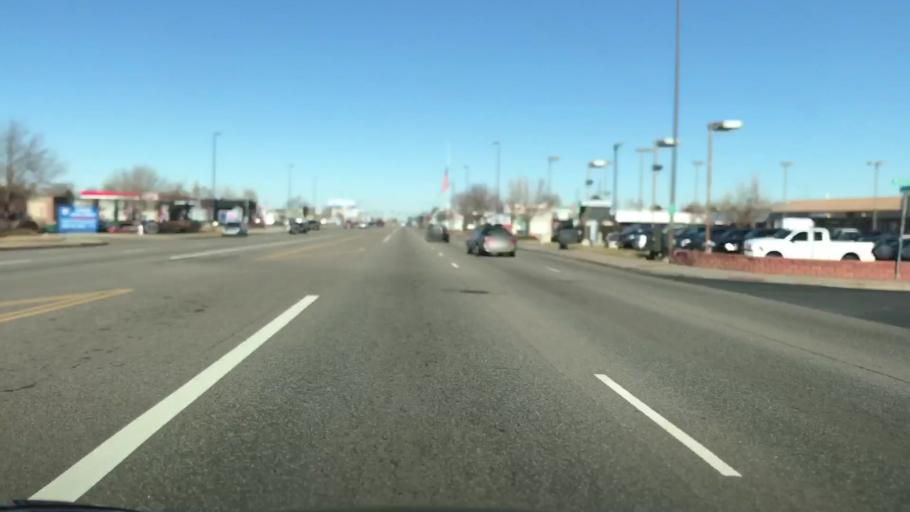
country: US
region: Colorado
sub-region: Adams County
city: Aurora
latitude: 39.7000
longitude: -104.8660
